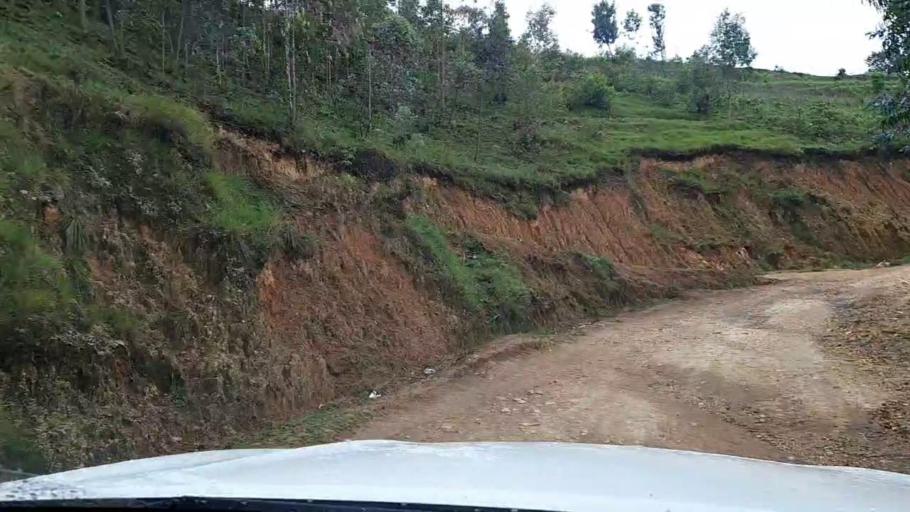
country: RW
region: Southern Province
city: Nzega
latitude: -2.4579
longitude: 29.4924
